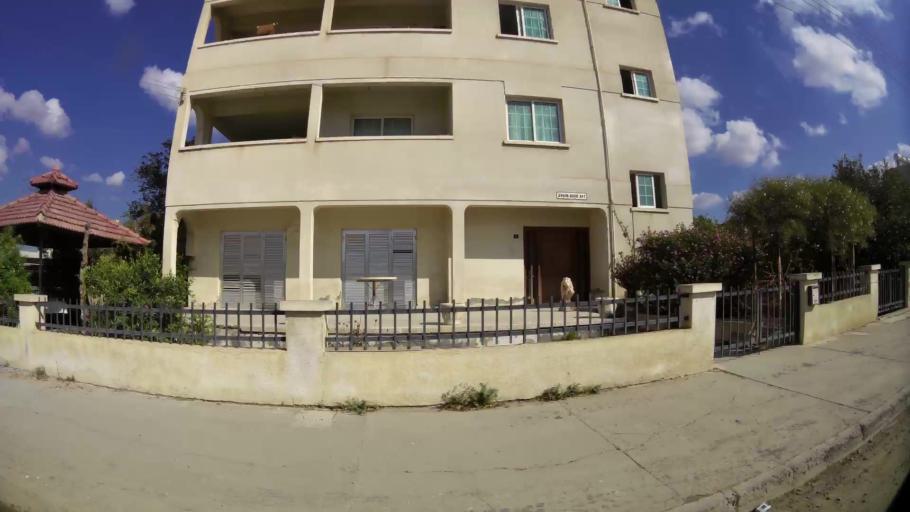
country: CY
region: Lefkosia
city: Nicosia
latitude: 35.2135
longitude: 33.3792
